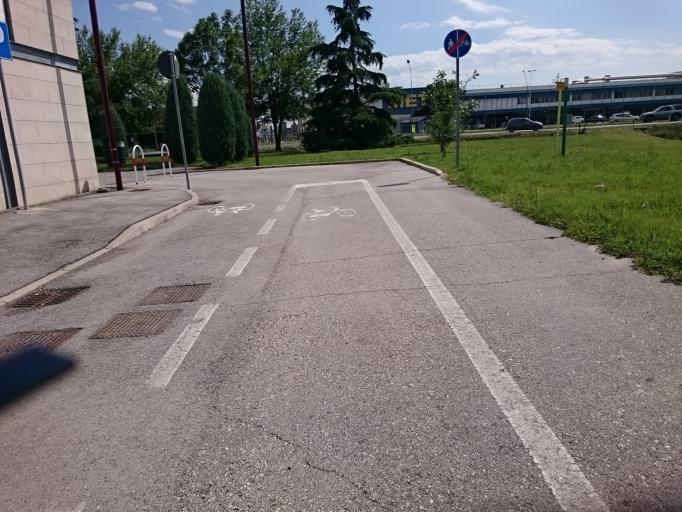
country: IT
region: Veneto
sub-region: Provincia di Padova
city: Rubano
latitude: 45.4242
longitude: 11.7983
